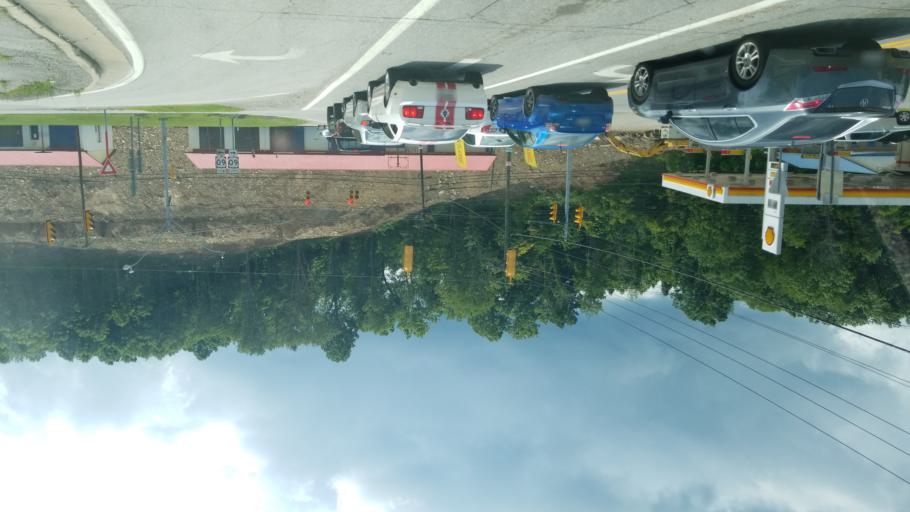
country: US
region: West Virginia
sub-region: Kanawha County
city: Nitro
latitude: 38.3976
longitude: -81.8561
